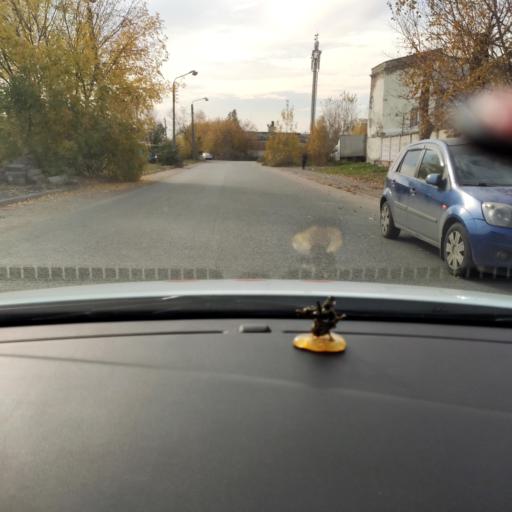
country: RU
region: Tatarstan
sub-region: Gorod Kazan'
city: Kazan
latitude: 55.7455
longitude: 49.1108
